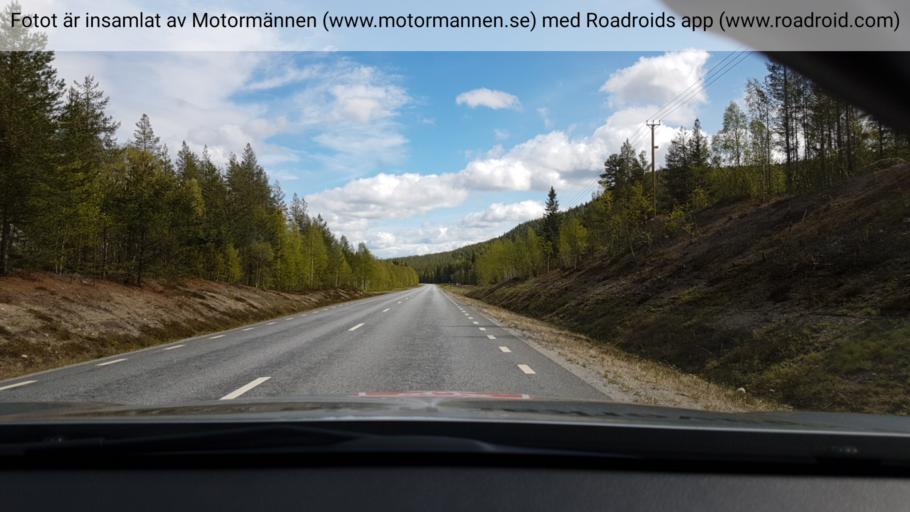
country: SE
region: Vaesterbotten
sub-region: Asele Kommun
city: Insjon
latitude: 64.1738
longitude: 17.7969
